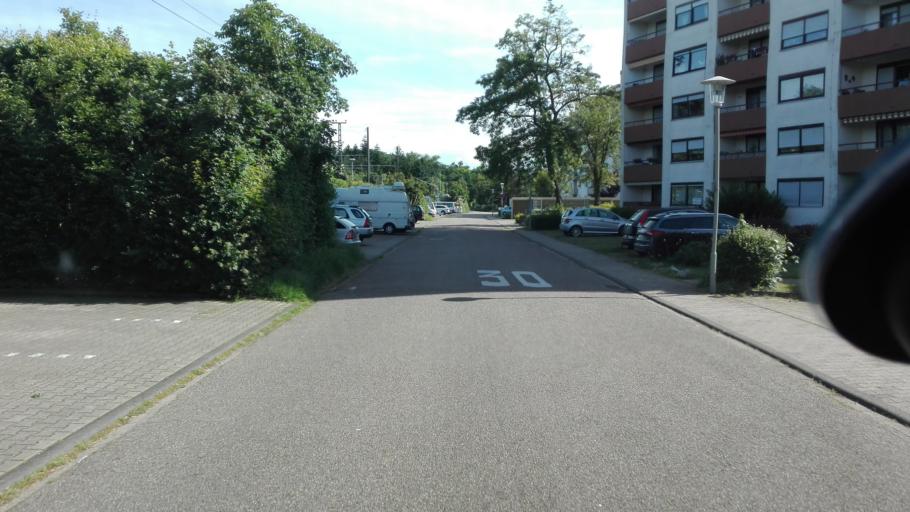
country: DE
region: Baden-Wuerttemberg
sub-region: Karlsruhe Region
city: Eggenstein-Leopoldshafen
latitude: 49.0993
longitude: 8.4026
